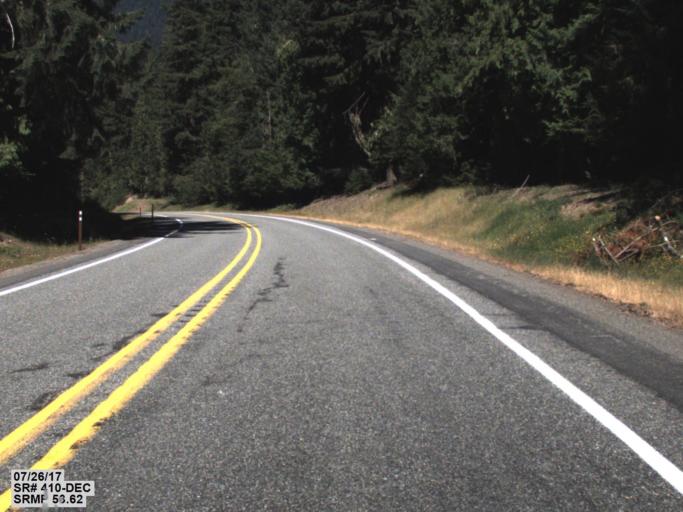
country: US
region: Washington
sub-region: King County
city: Enumclaw
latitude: 47.0292
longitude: -121.5478
